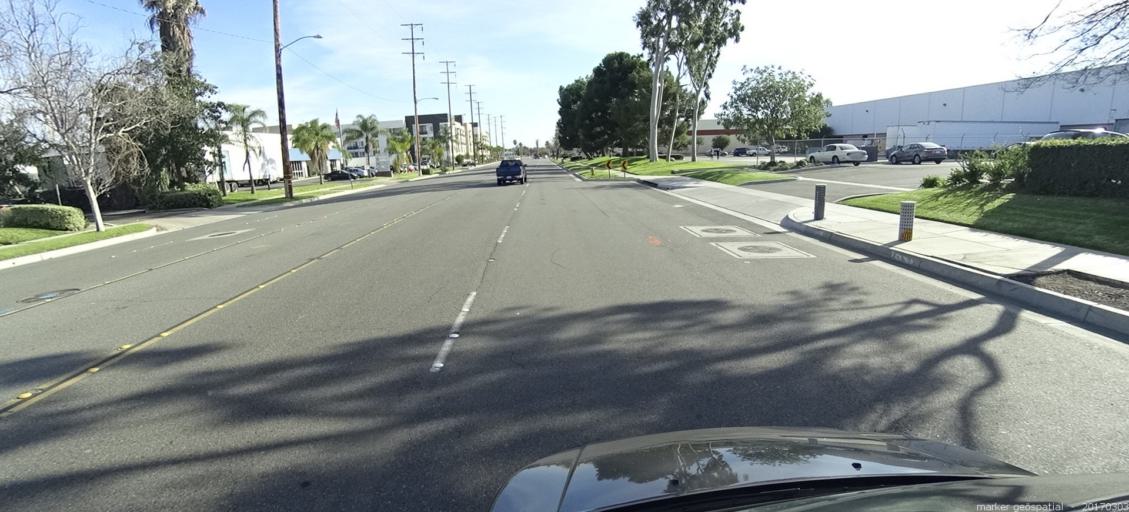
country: US
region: California
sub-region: Orange County
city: Anaheim
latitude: 33.8067
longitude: -117.8980
